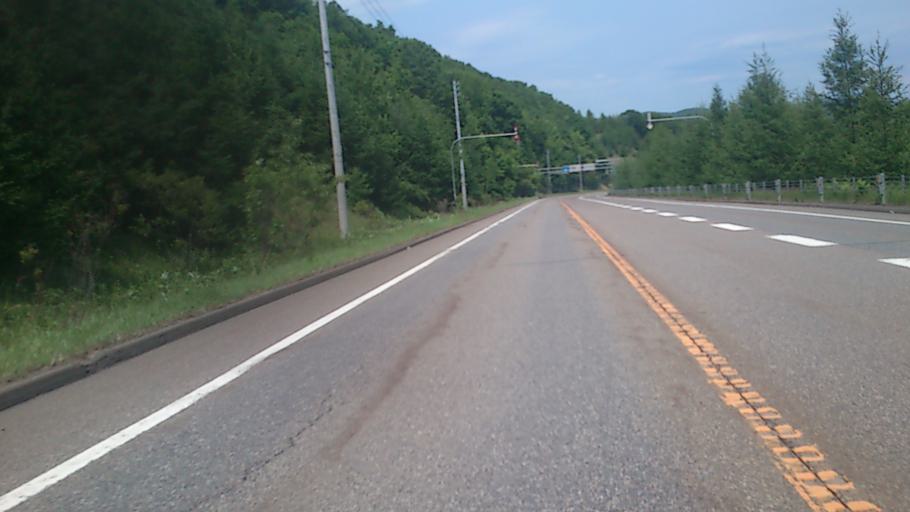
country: JP
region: Hokkaido
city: Otofuke
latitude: 43.2351
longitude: 143.5282
